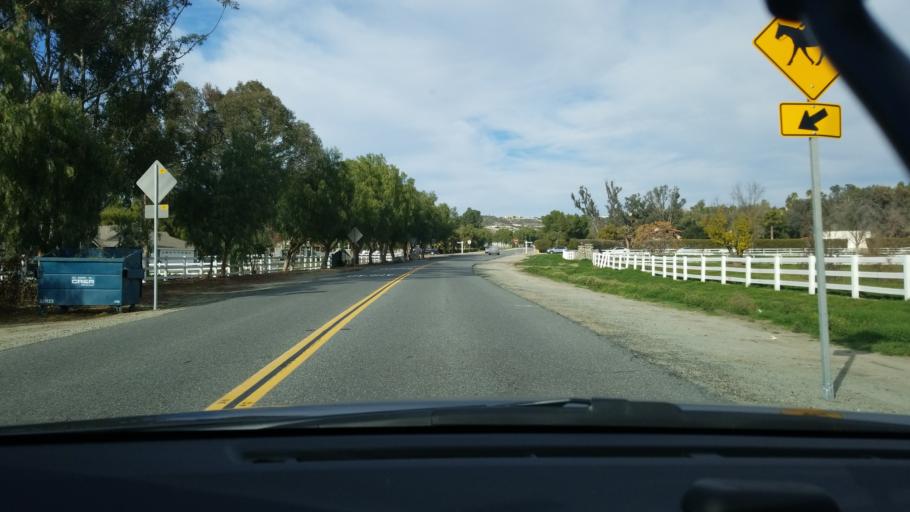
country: US
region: California
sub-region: Riverside County
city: Temecula
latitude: 33.4772
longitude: -117.1227
